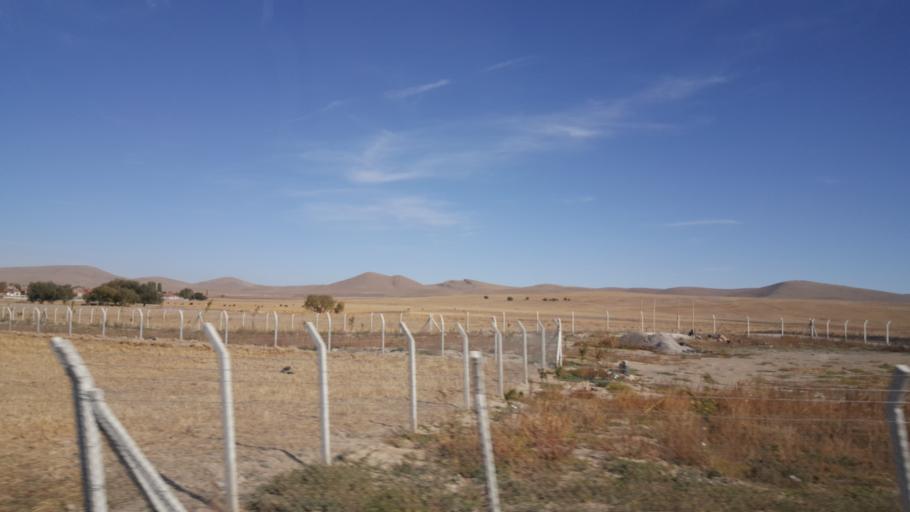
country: TR
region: Ankara
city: Altpinar
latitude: 39.2550
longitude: 32.7525
